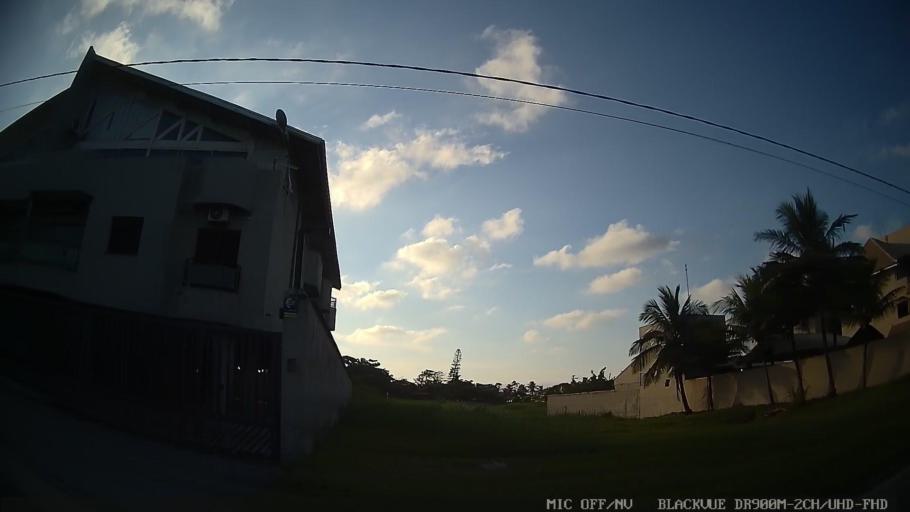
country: BR
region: Sao Paulo
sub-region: Peruibe
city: Peruibe
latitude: -24.3016
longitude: -46.9694
